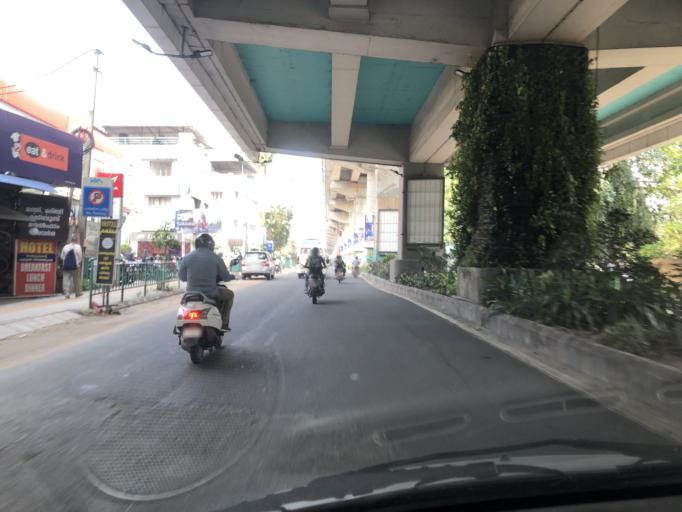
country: IN
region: Kerala
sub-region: Ernakulam
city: Elur
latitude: 10.0064
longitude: 76.3047
